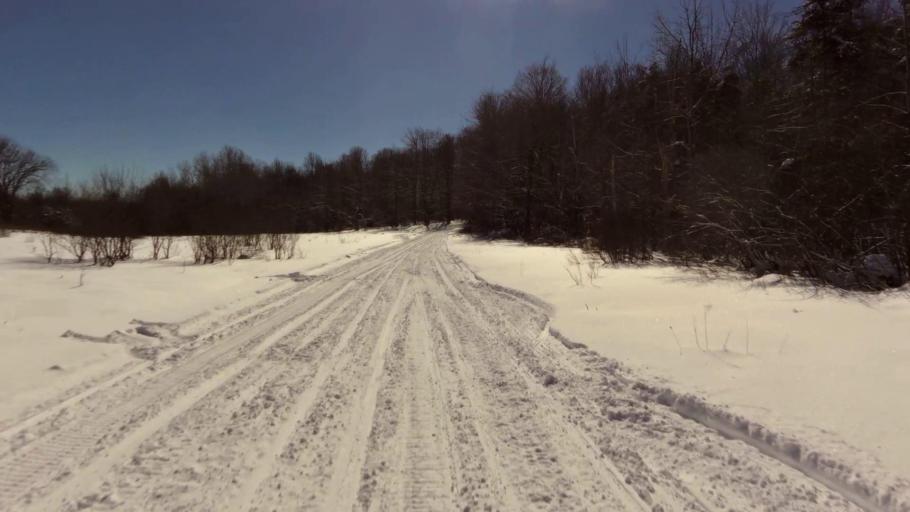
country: US
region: New York
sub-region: Chautauqua County
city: Mayville
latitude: 42.2155
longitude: -79.5347
